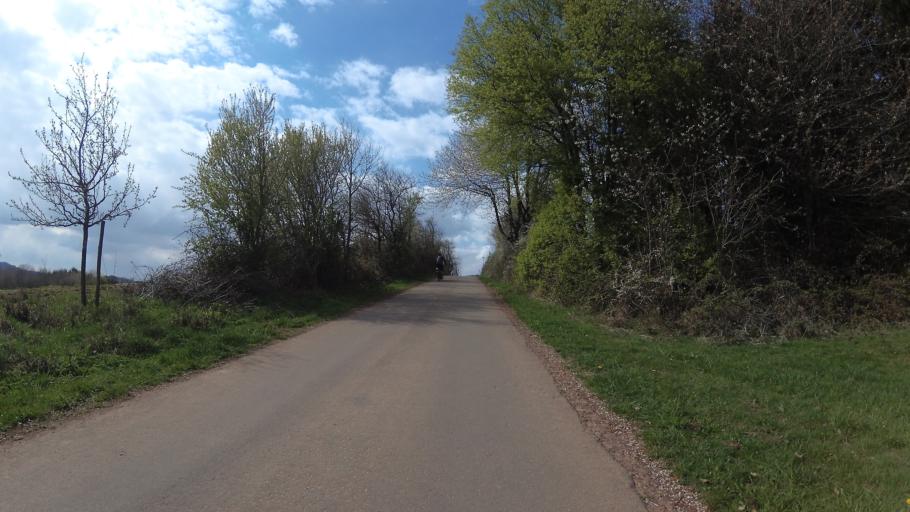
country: DE
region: Saarland
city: Oberthal
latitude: 49.5139
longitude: 7.1154
